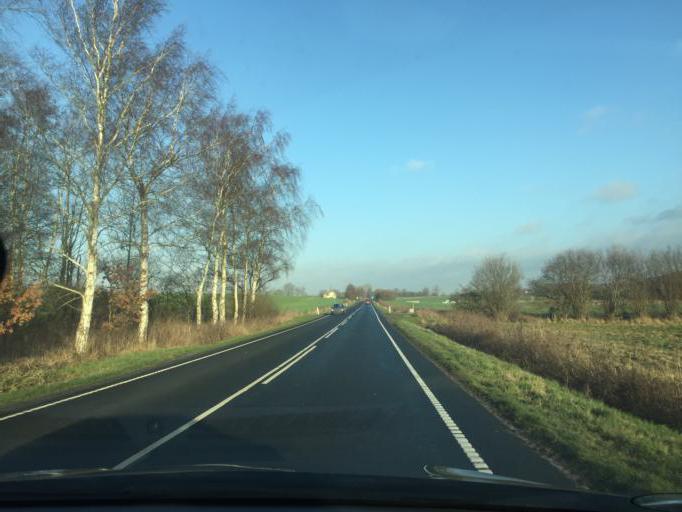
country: DK
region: South Denmark
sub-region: Faaborg-Midtfyn Kommune
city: Faaborg
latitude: 55.1735
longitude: 10.2899
